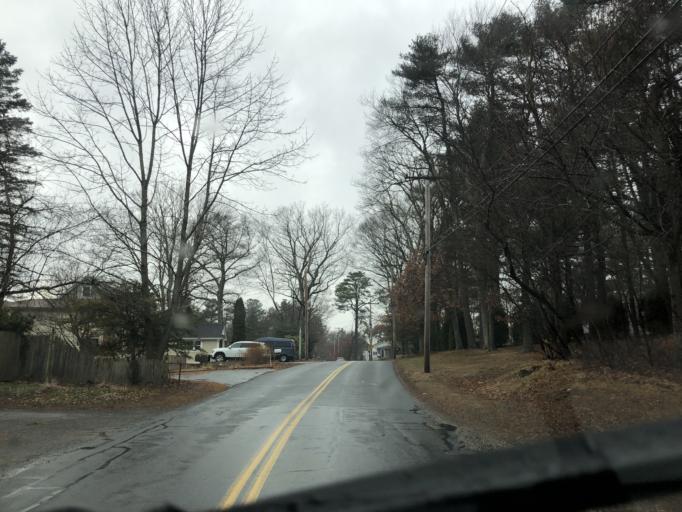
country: US
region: Massachusetts
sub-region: Norfolk County
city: Plainville
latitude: 42.0042
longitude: -71.2776
